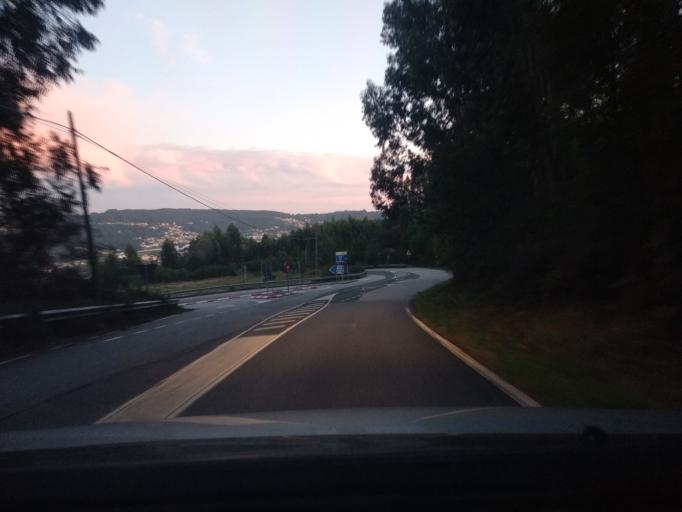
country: ES
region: Galicia
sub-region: Provincia de Pontevedra
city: Moana
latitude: 42.2946
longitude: -8.6936
